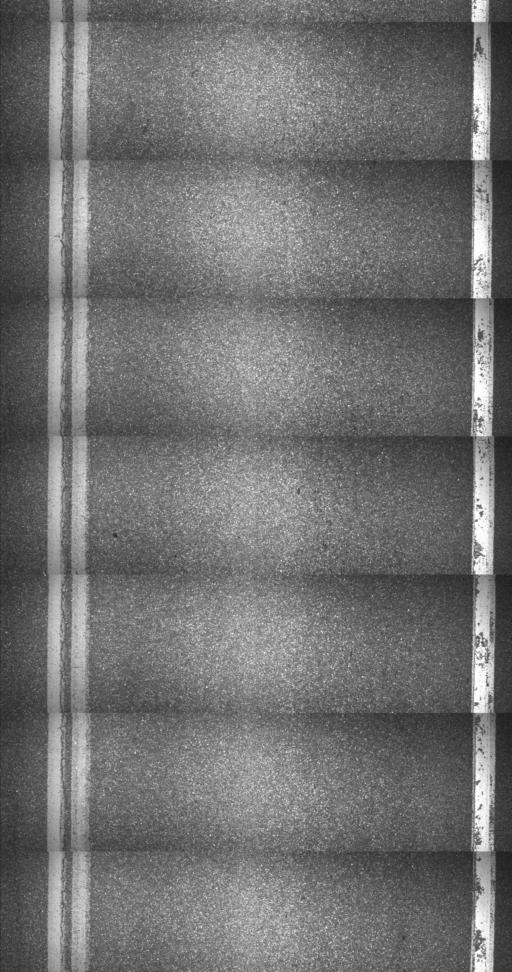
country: US
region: Vermont
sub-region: Chittenden County
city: Milton
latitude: 44.6948
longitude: -73.0351
